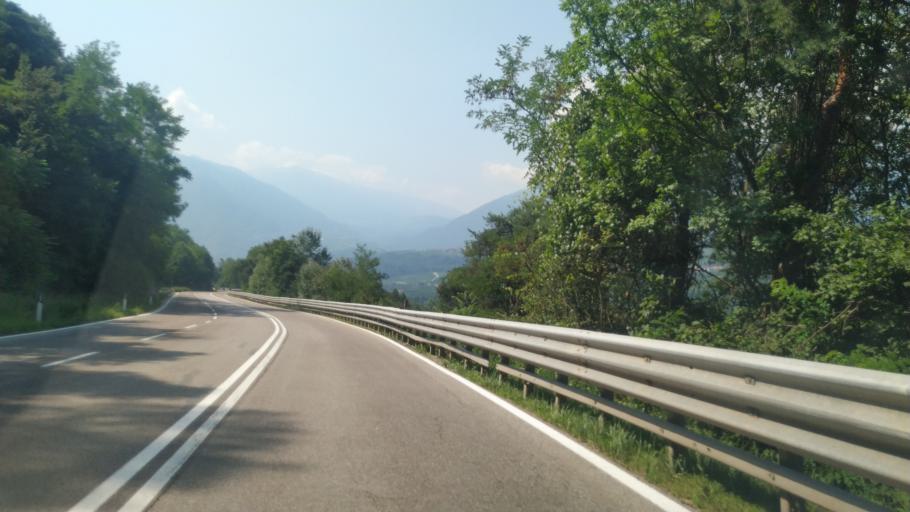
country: IT
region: Trentino-Alto Adige
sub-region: Provincia di Trento
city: Denno
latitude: 46.2881
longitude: 11.0626
